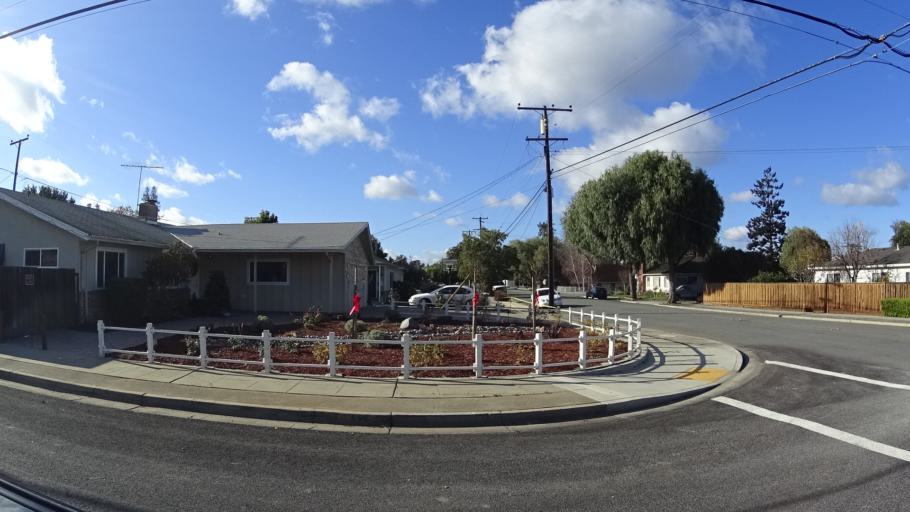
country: US
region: California
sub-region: Santa Clara County
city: Sunnyvale
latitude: 37.3747
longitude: -122.0435
